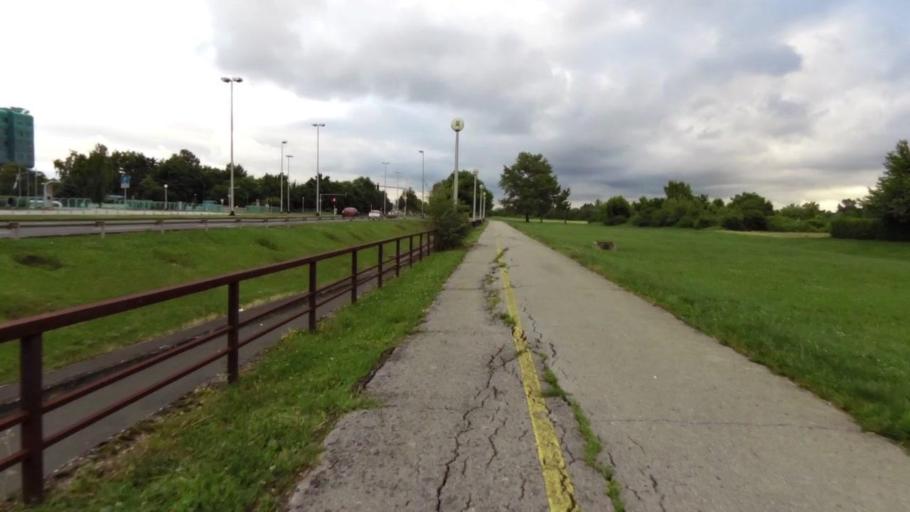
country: HR
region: Grad Zagreb
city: Dubrava
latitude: 45.8351
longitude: 16.0328
